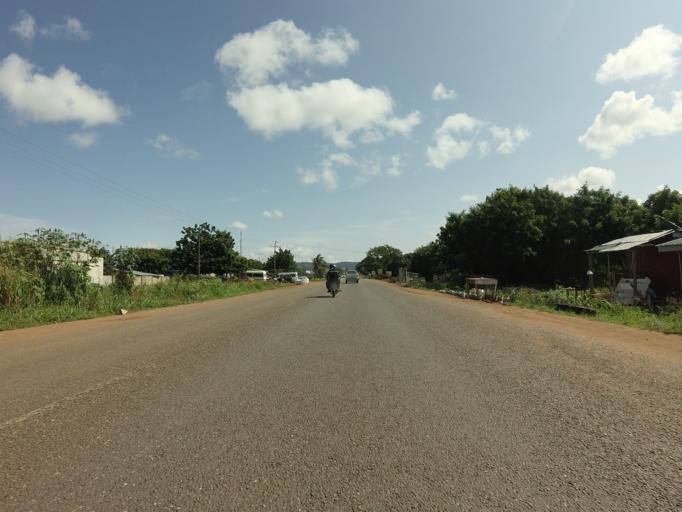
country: GH
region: Eastern
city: Aburi
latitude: 5.8510
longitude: -0.1133
